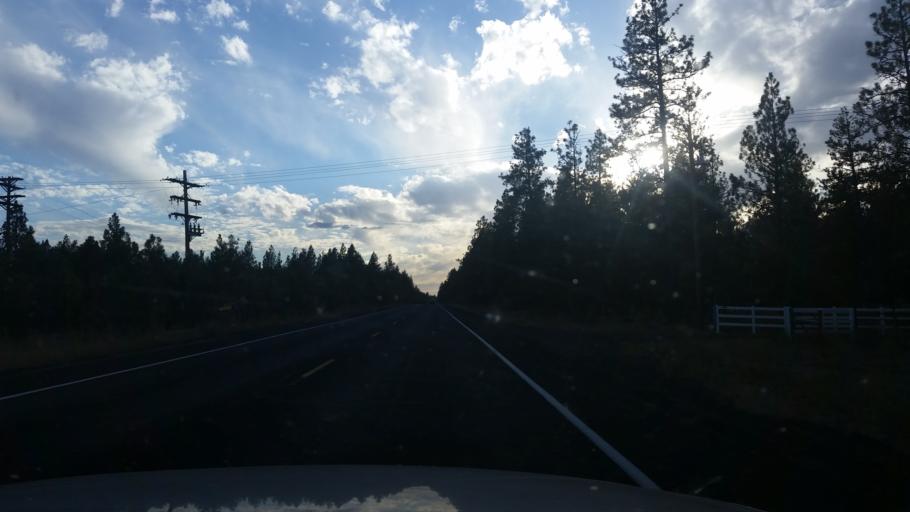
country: US
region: Washington
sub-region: Spokane County
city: Cheney
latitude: 47.4611
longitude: -117.6819
